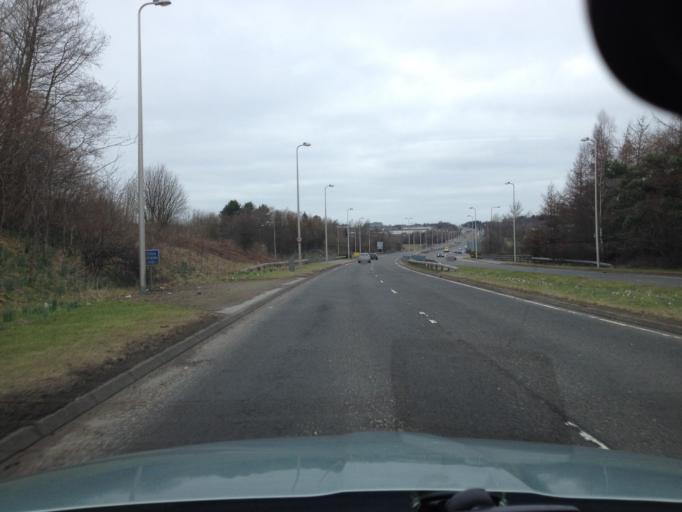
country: GB
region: Scotland
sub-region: West Lothian
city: Mid Calder
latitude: 55.8859
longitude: -3.4992
